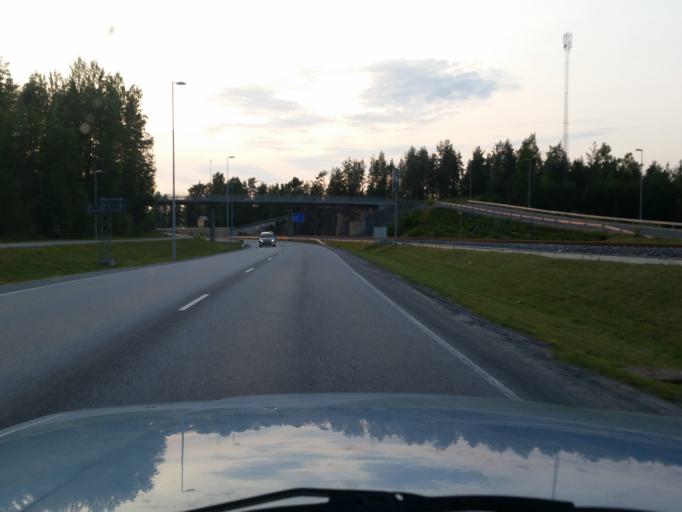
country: FI
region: Southern Savonia
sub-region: Savonlinna
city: Savonlinna
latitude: 61.8777
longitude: 28.8730
